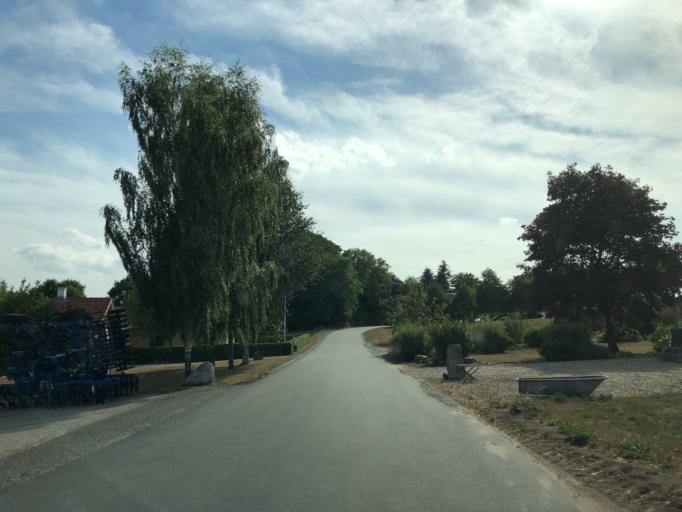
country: DK
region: South Denmark
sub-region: Vejle Kommune
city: Egtved
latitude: 55.6712
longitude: 9.2689
